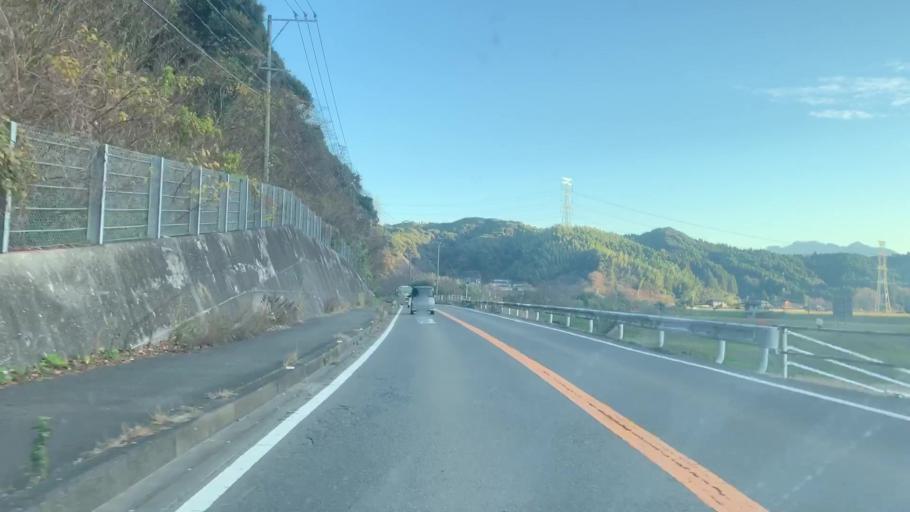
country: JP
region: Saga Prefecture
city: Karatsu
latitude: 33.3653
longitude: 130.0064
